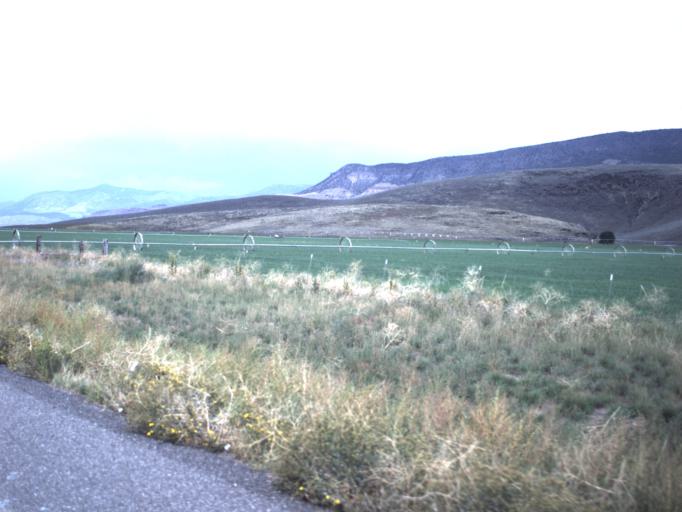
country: US
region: Utah
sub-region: Piute County
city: Junction
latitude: 38.2482
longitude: -112.2202
